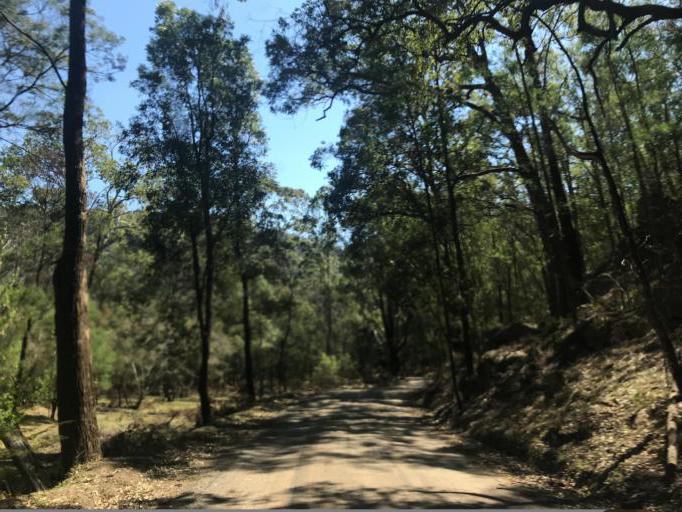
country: AU
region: New South Wales
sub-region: Wyong Shire
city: Little Jilliby
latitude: -33.1960
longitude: 151.0162
